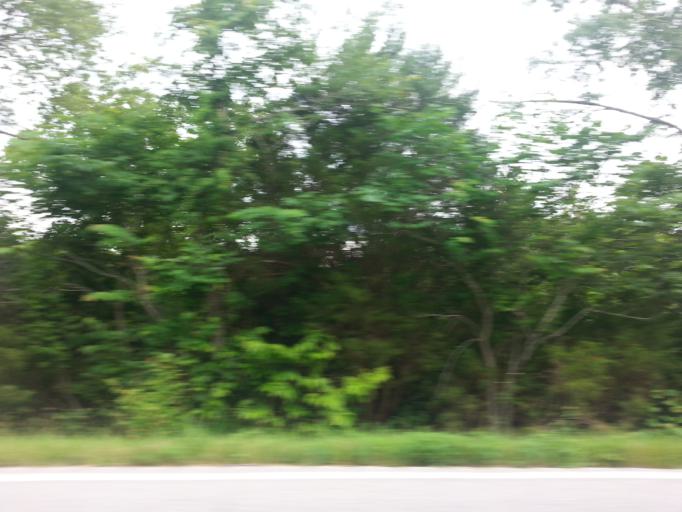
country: US
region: Kentucky
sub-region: Harrison County
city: Cynthiana
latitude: 38.4862
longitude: -84.2136
